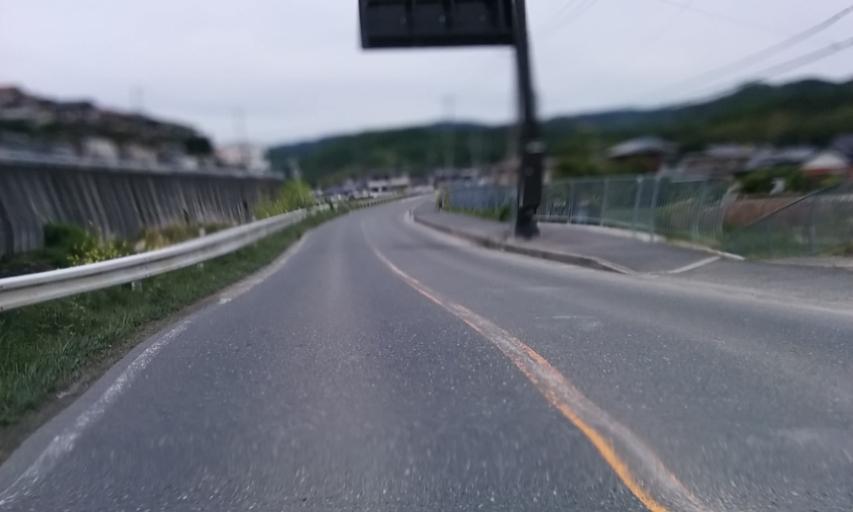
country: JP
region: Osaka
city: Takatsuki
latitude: 34.8702
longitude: 135.6256
